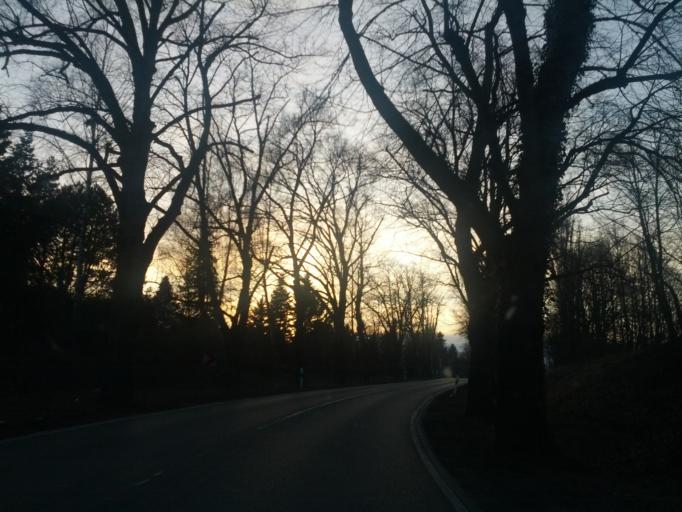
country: DE
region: Thuringia
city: Muehlhausen
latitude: 51.2049
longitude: 10.4204
